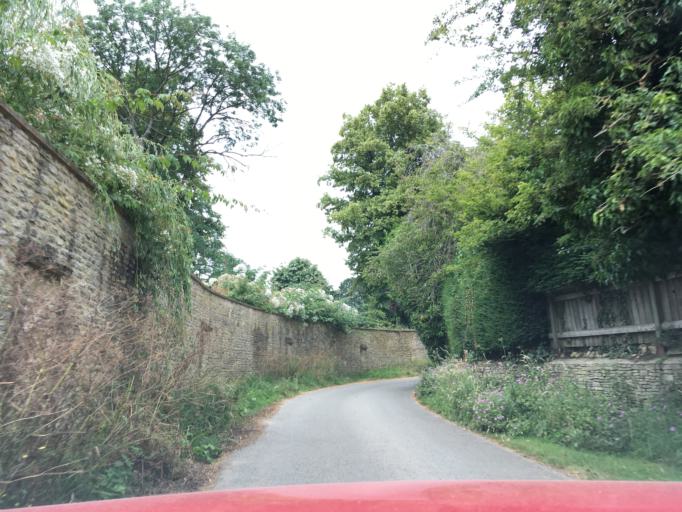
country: GB
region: England
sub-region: Oxfordshire
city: Charlbury
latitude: 51.9013
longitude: -1.5022
